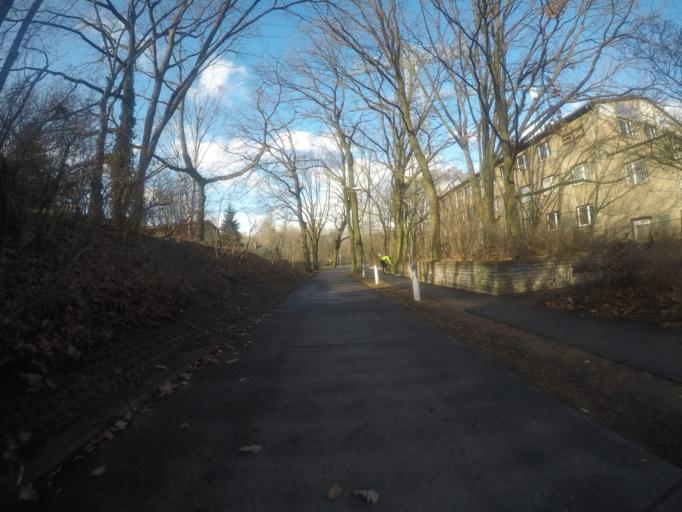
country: DE
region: Berlin
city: Karlshorst
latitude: 52.4973
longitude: 13.5404
